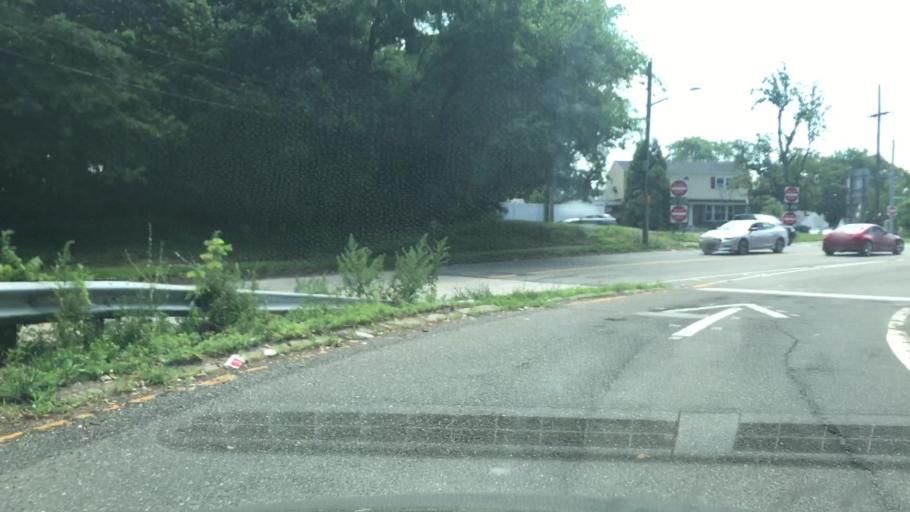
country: US
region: New York
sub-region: Nassau County
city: North Valley Stream
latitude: 40.6863
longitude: -73.7152
